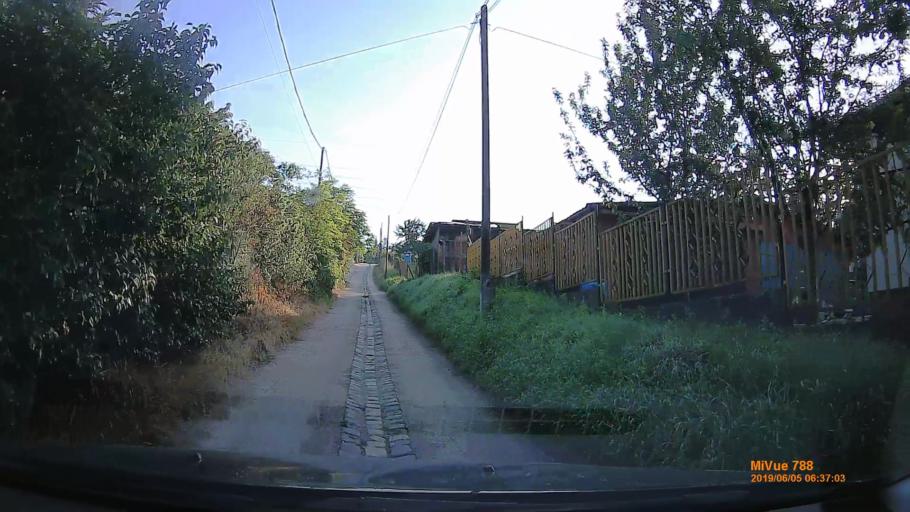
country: HU
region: Pest
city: Urom
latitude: 47.5763
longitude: 19.0190
